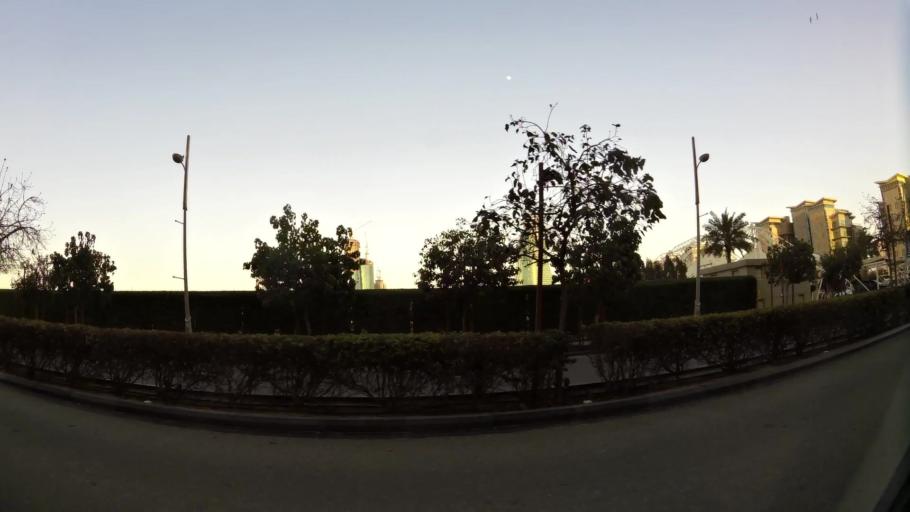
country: BH
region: Manama
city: Jidd Hafs
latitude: 26.2376
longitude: 50.5633
